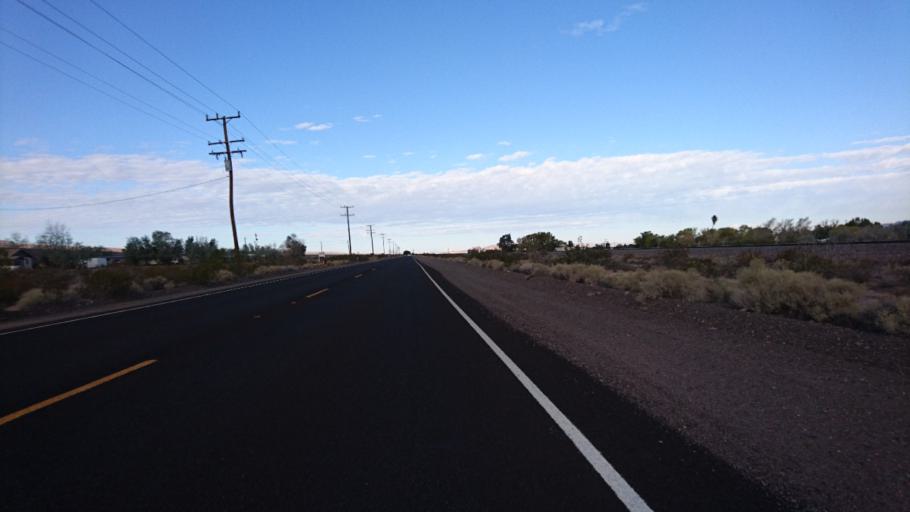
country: US
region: California
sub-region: San Bernardino County
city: Barstow
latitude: 34.8429
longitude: -116.7577
